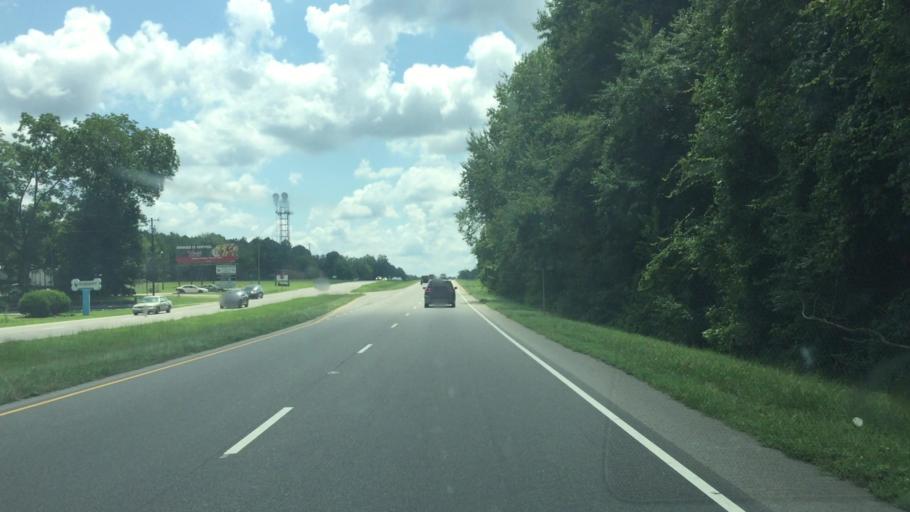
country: US
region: North Carolina
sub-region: Scotland County
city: Laurel Hill
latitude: 34.7967
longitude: -79.5176
